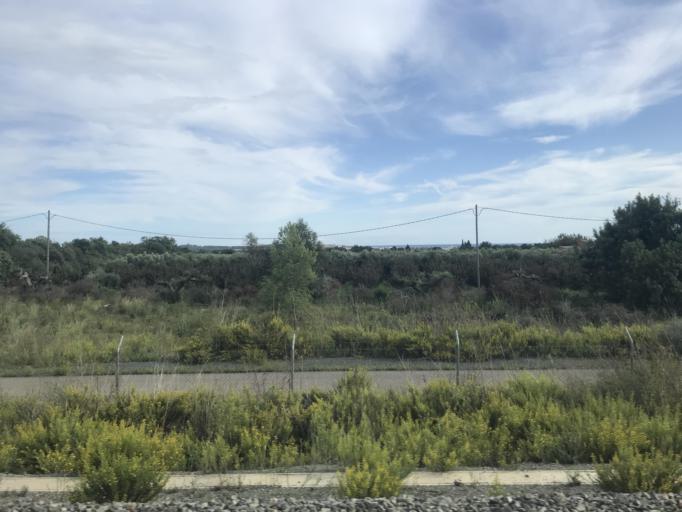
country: ES
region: Catalonia
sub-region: Provincia de Tarragona
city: Vila-seca
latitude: 41.1062
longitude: 1.1034
